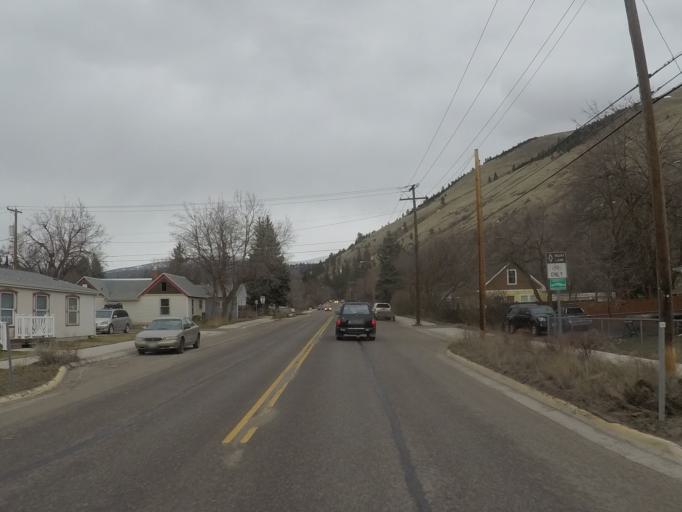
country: US
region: Montana
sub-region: Missoula County
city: Missoula
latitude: 46.8728
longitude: -113.9779
